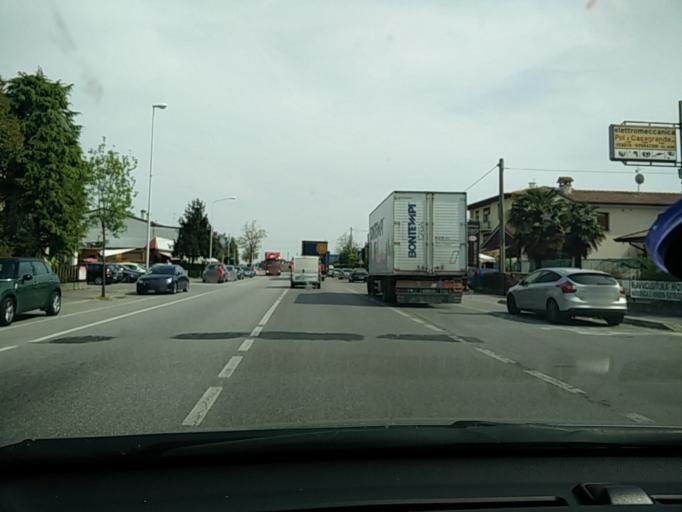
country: IT
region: Veneto
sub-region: Provincia di Treviso
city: San Vendemiano-Fossamerlo
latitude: 45.8792
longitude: 12.3282
